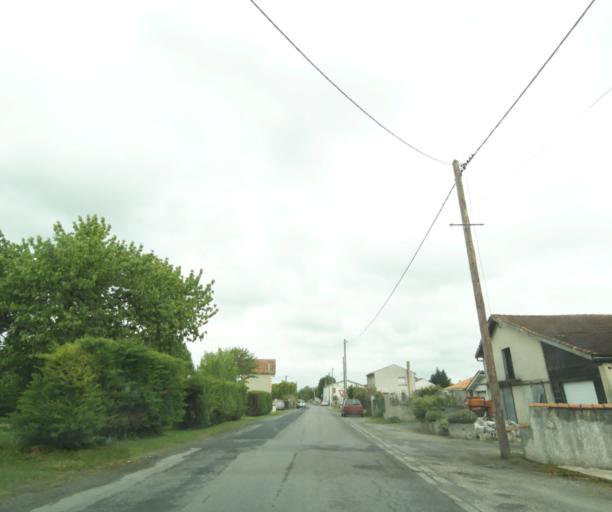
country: FR
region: Poitou-Charentes
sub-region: Departement de la Charente-Maritime
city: Chaniers
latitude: 45.6964
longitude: -0.5258
